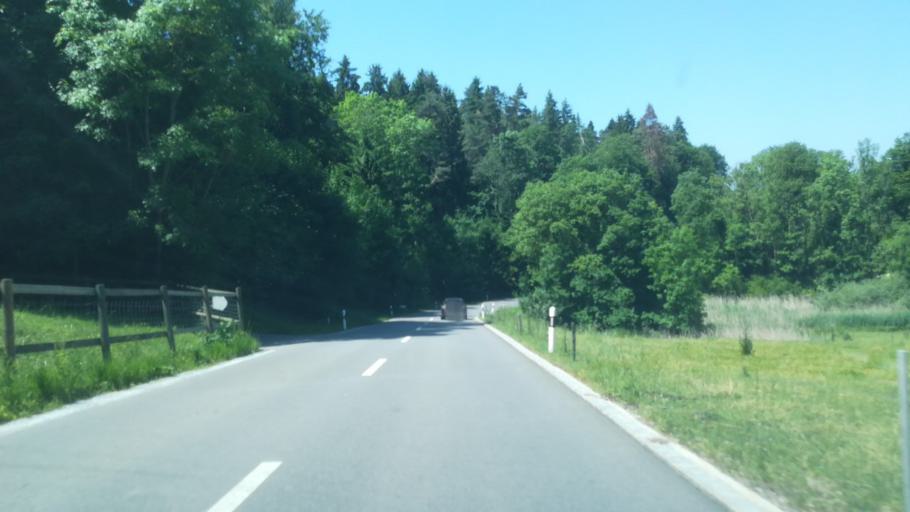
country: CH
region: Thurgau
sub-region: Frauenfeld District
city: Pfyn
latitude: 47.6321
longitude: 8.9241
